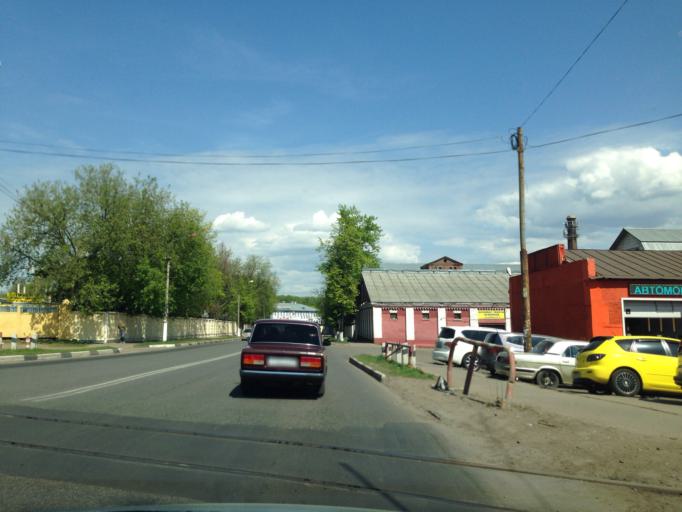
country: RU
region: Moskovskaya
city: Balashikha
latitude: 55.8116
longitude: 37.9532
